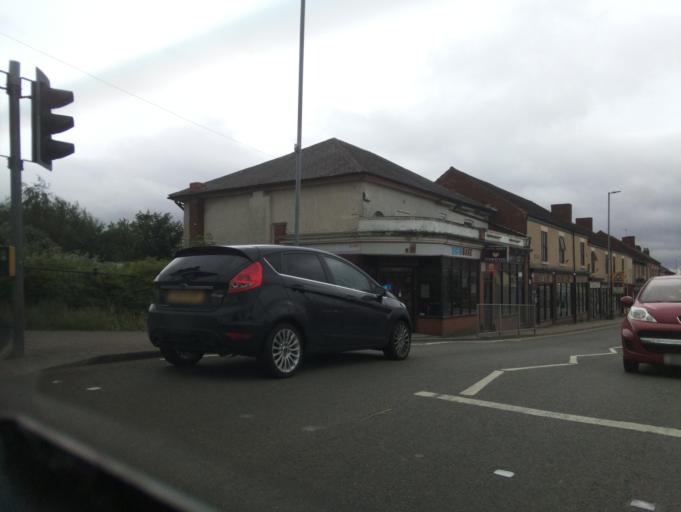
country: GB
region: England
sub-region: Leicestershire
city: Coalville
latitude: 52.7238
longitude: -1.3687
